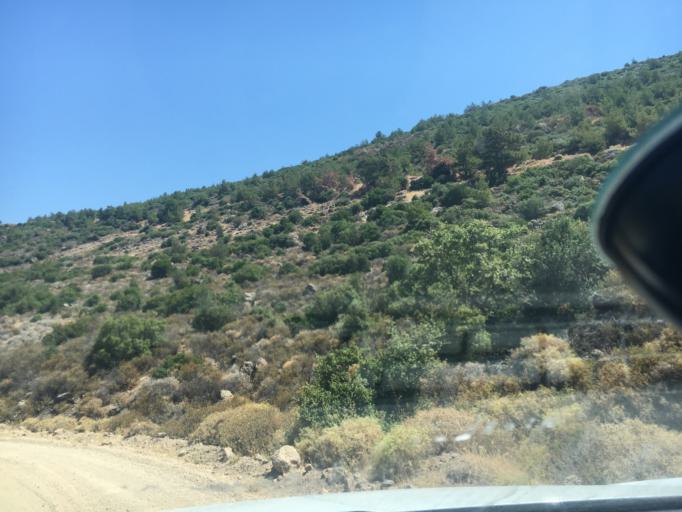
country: TR
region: Canakkale
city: Gulpinar
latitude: 39.4818
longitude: 26.0732
